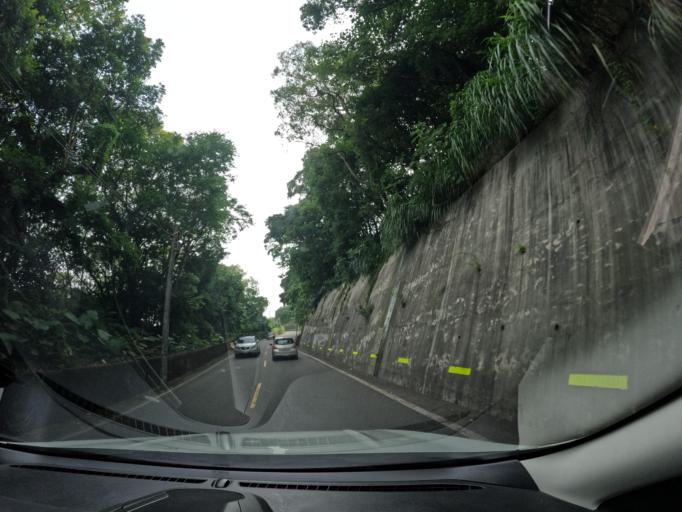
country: TW
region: Taiwan
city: Daxi
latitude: 24.9287
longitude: 121.3060
